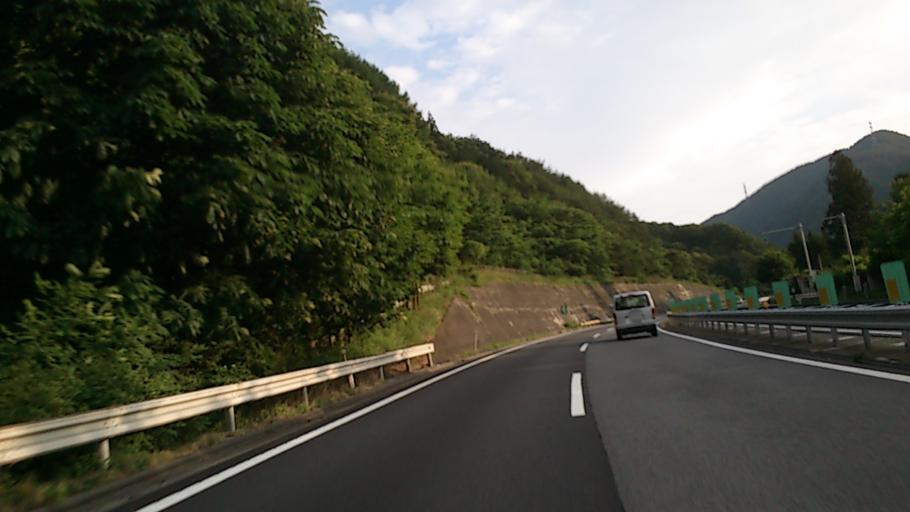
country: JP
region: Nagano
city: Okaya
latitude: 36.0253
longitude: 138.0211
